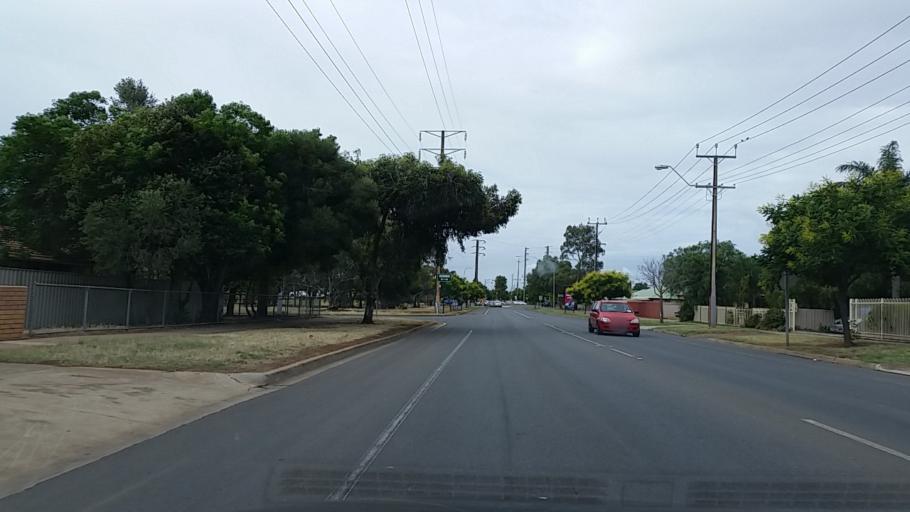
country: AU
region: South Australia
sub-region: Playford
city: Smithfield
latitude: -34.6761
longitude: 138.6836
